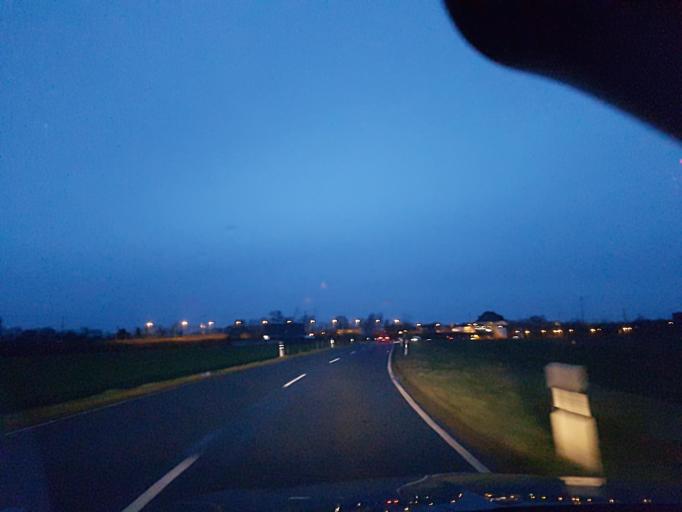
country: DE
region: Brandenburg
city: Doberlug-Kirchhain
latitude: 51.6181
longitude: 13.5676
